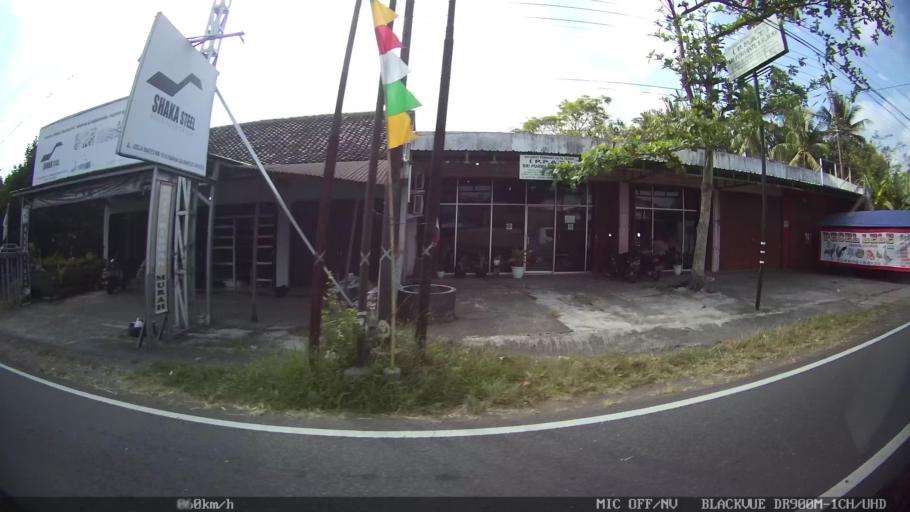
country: ID
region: Daerah Istimewa Yogyakarta
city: Srandakan
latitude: -7.8417
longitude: 110.2190
